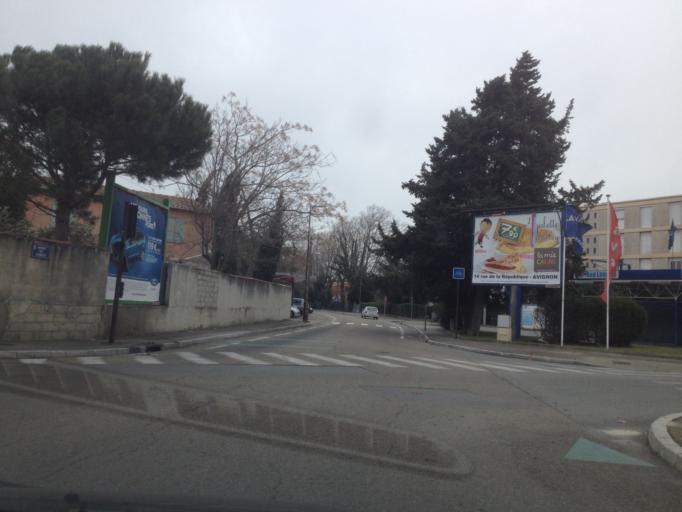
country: FR
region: Provence-Alpes-Cote d'Azur
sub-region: Departement du Vaucluse
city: Avignon
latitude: 43.9322
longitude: 4.8204
